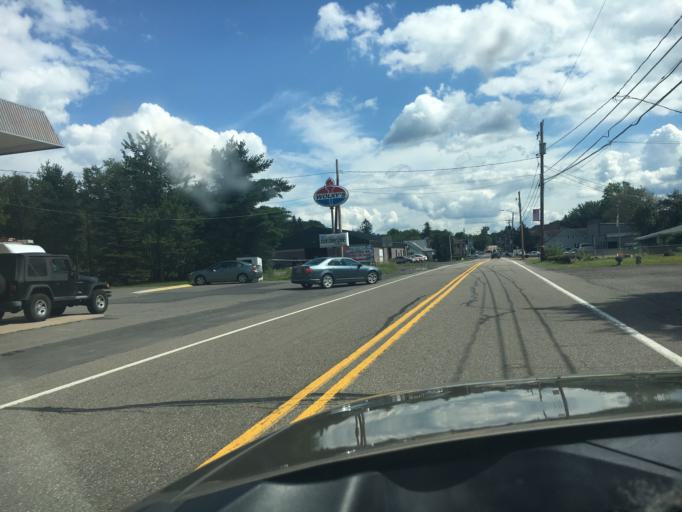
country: US
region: Pennsylvania
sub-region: Schuylkill County
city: Mahanoy City
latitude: 40.9005
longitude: -76.1186
